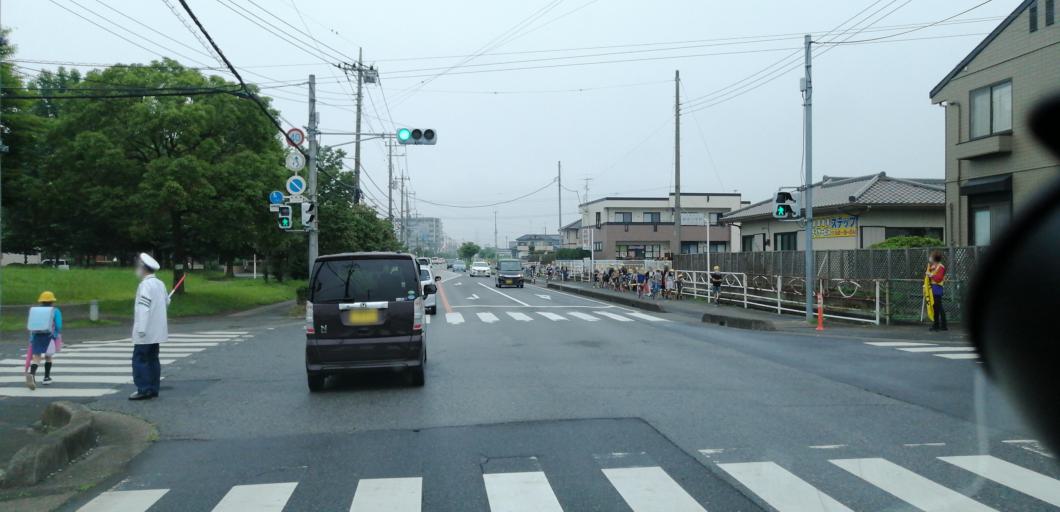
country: JP
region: Saitama
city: Kukichuo
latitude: 36.0912
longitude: 139.6862
